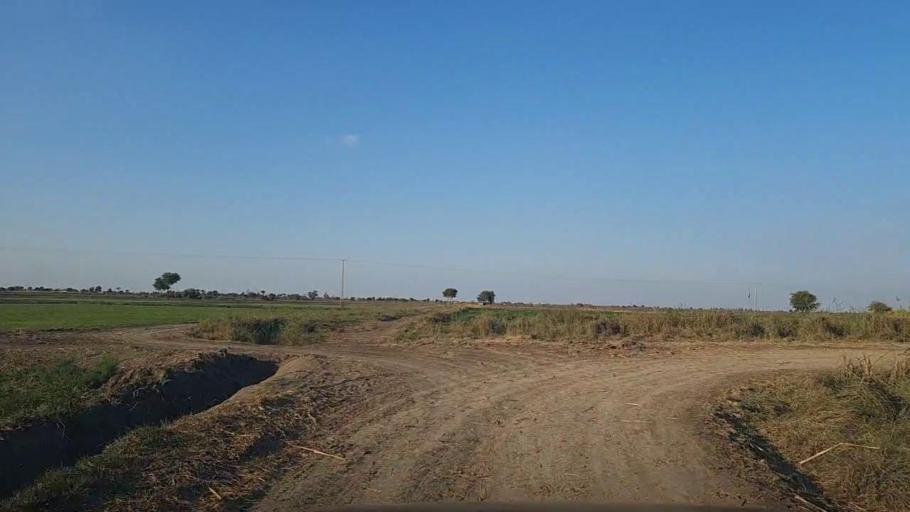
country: PK
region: Sindh
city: Sanghar
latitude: 25.9237
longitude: 69.0522
